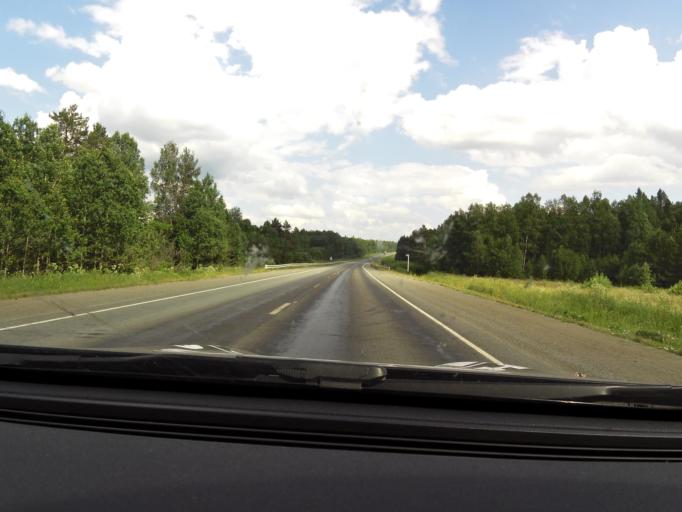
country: RU
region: Sverdlovsk
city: Bisert'
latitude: 56.8351
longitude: 58.9221
